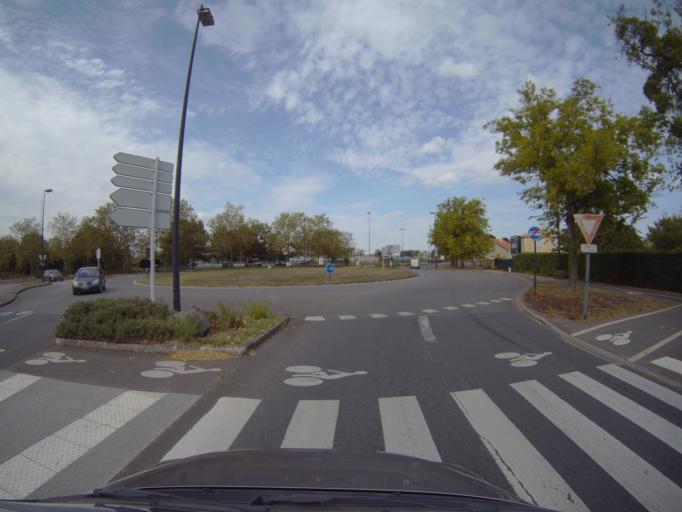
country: FR
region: Pays de la Loire
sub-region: Departement de la Loire-Atlantique
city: Bouguenais
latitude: 47.2005
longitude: -1.6133
